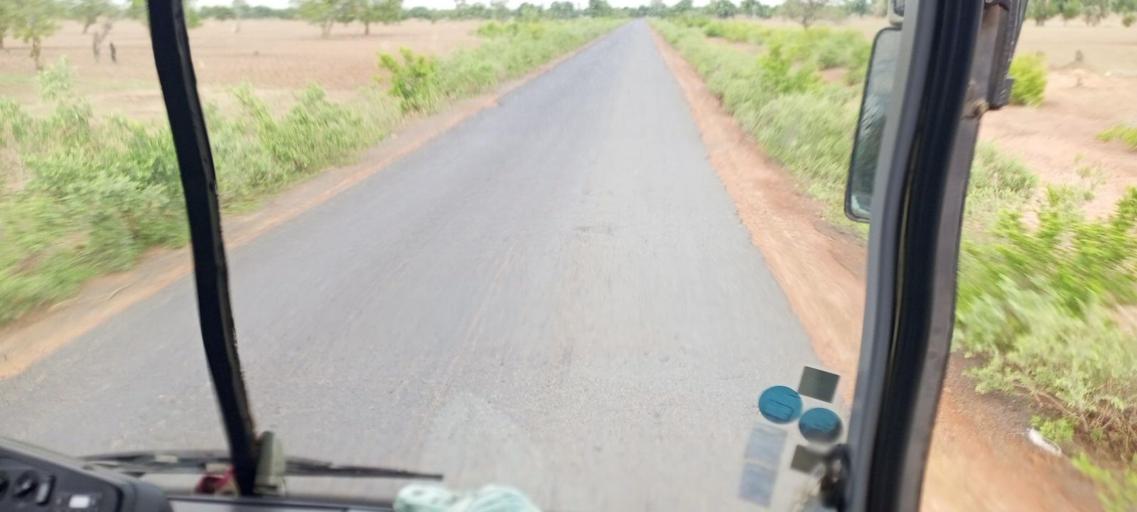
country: ML
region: Segou
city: Bla
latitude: 12.7437
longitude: -5.7300
